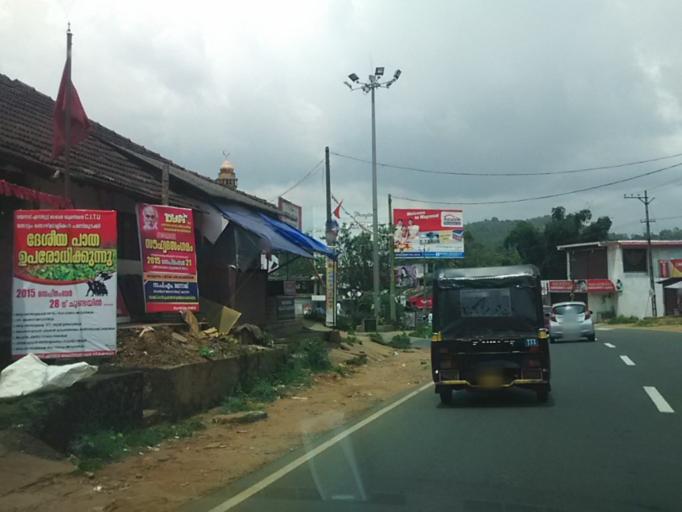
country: IN
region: Kerala
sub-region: Wayanad
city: Kalpetta
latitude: 11.5525
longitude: 76.0389
